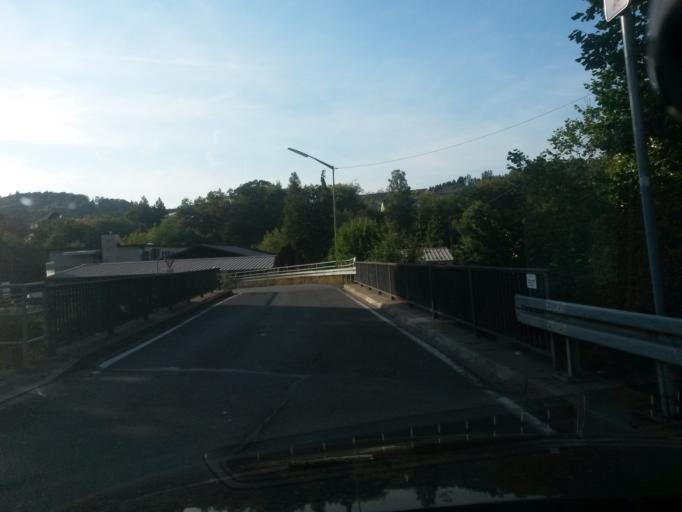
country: DE
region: North Rhine-Westphalia
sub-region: Regierungsbezirk Koln
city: Gummersbach
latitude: 51.0032
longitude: 7.5786
